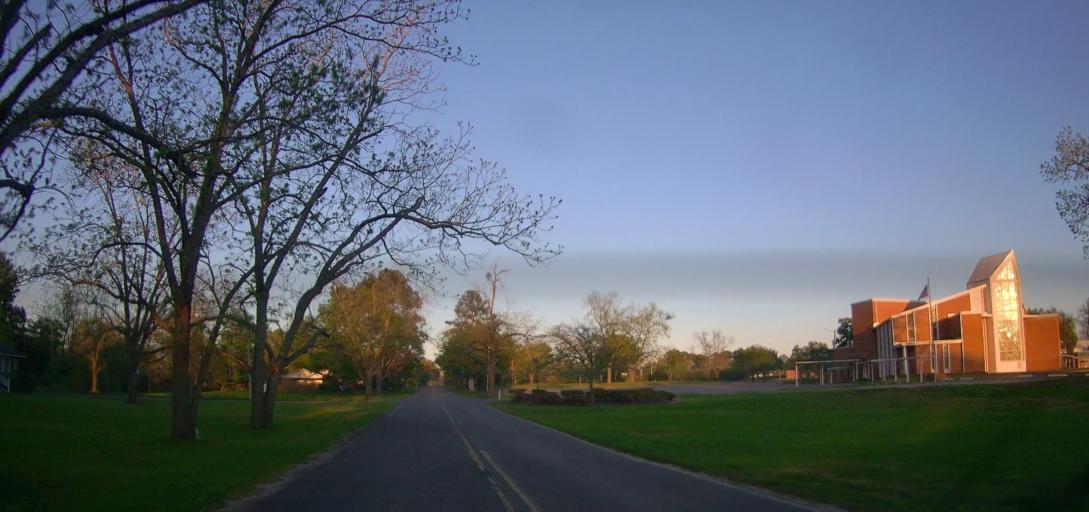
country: US
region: Georgia
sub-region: Ben Hill County
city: Fitzgerald
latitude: 31.7112
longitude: -83.2641
